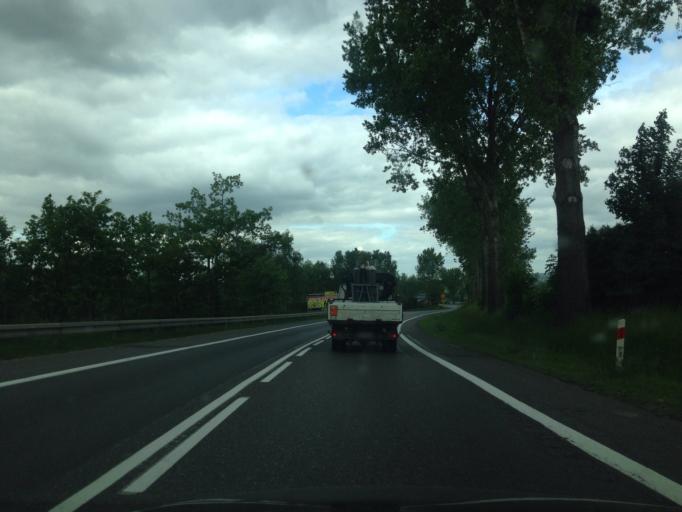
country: PL
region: Kujawsko-Pomorskie
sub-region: Powiat chelminski
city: Chelmno
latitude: 53.3477
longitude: 18.4529
